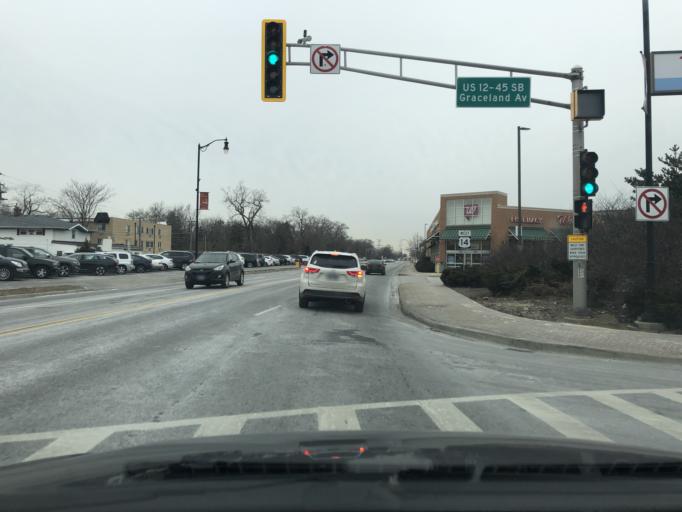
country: US
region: Illinois
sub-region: Cook County
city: Des Plaines
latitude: 42.0424
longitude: -87.8893
